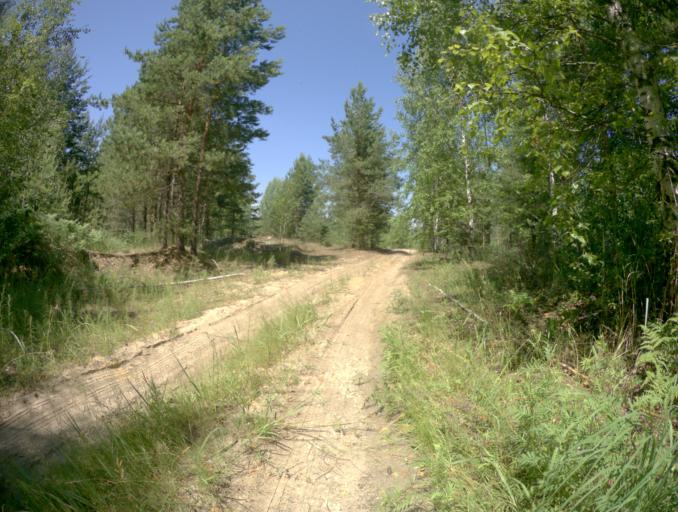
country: RU
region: Ivanovo
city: Talitsy
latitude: 56.4455
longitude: 42.2342
